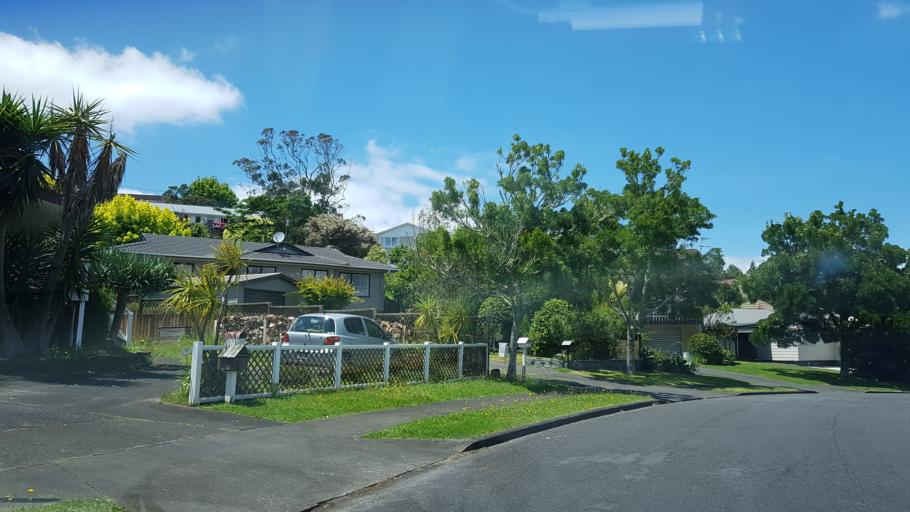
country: NZ
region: Auckland
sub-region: Auckland
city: North Shore
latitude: -36.7854
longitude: 174.7198
